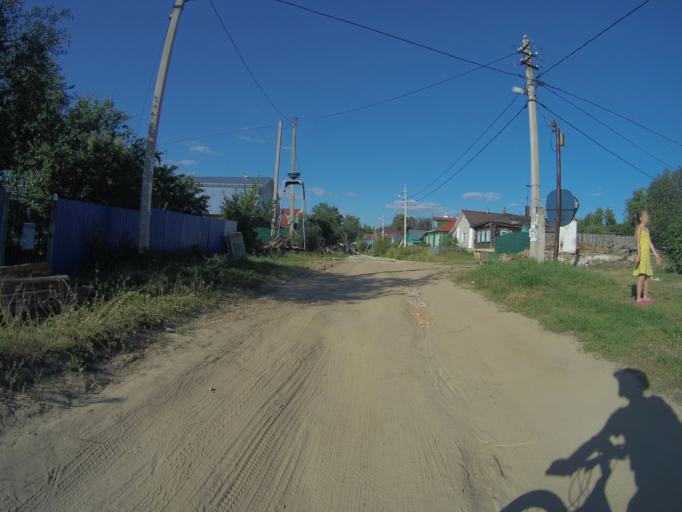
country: RU
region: Vladimir
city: Kommunar
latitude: 56.1185
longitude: 40.4995
